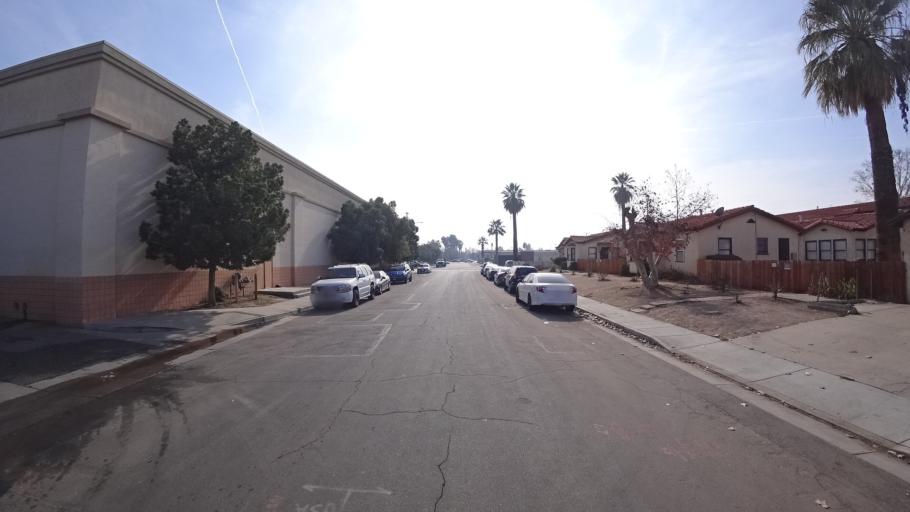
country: US
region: California
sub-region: Kern County
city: Bakersfield
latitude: 35.3558
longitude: -119.0202
